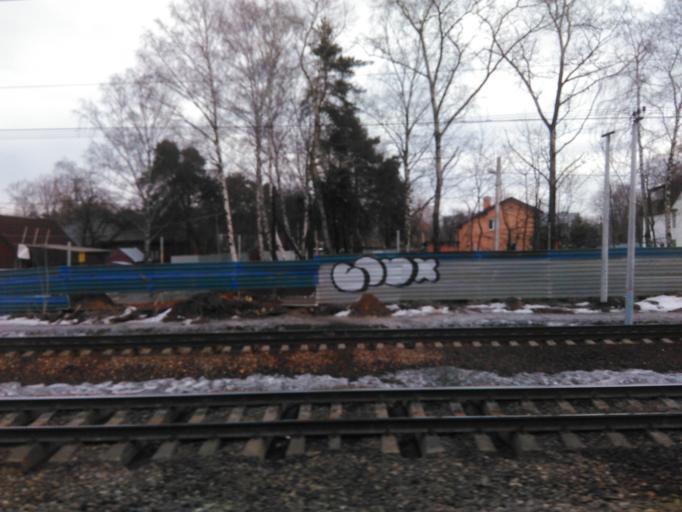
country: RU
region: Moskovskaya
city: Mytishchi
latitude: 55.9036
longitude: 37.7462
